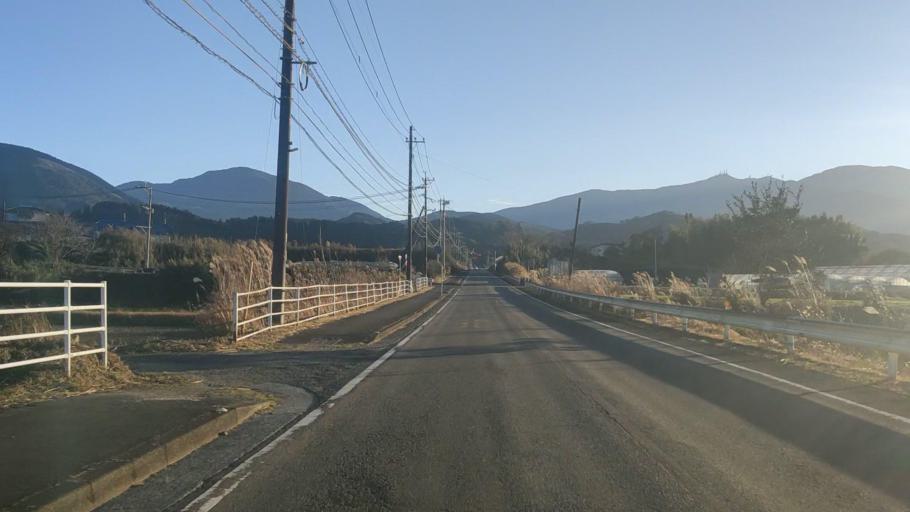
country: JP
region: Miyazaki
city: Miyazaki-shi
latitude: 31.8274
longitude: 131.2987
